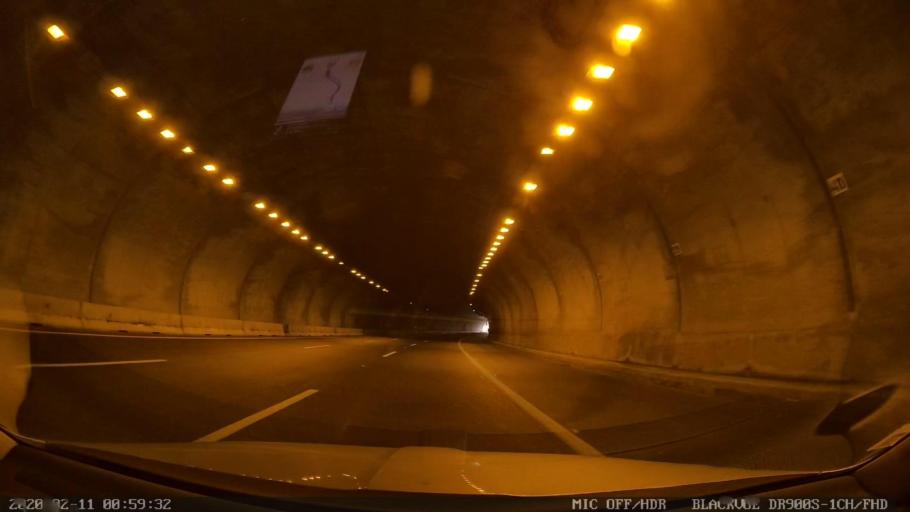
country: PT
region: Lisbon
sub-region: Arruda Dos Vinhos
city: Arruda dos Vinhos
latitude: 38.9431
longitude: -9.0674
